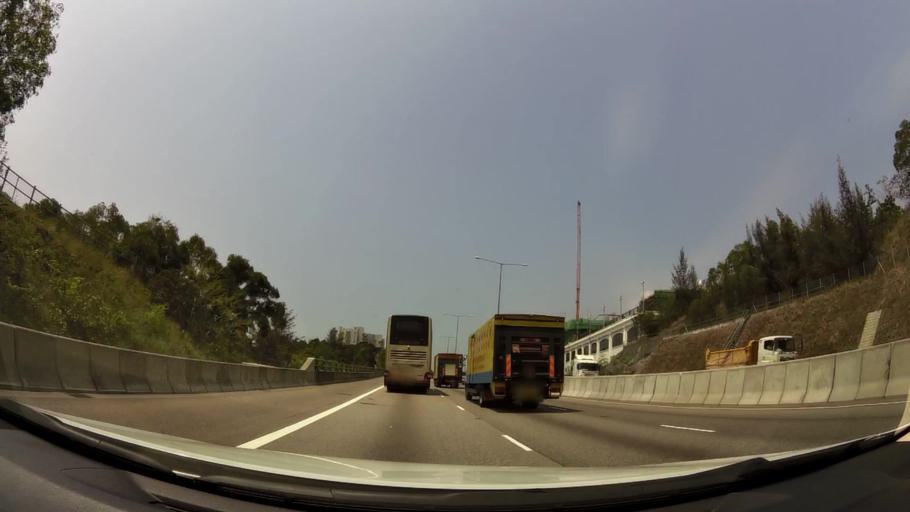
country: HK
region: Tuen Mun
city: Tuen Mun
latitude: 22.3754
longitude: 113.9921
